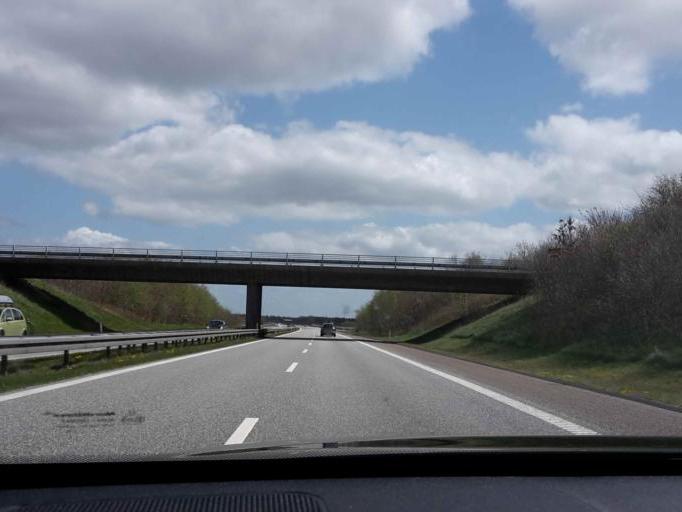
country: DK
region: South Denmark
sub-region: Esbjerg Kommune
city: Bramming
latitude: 55.5051
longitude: 8.6972
